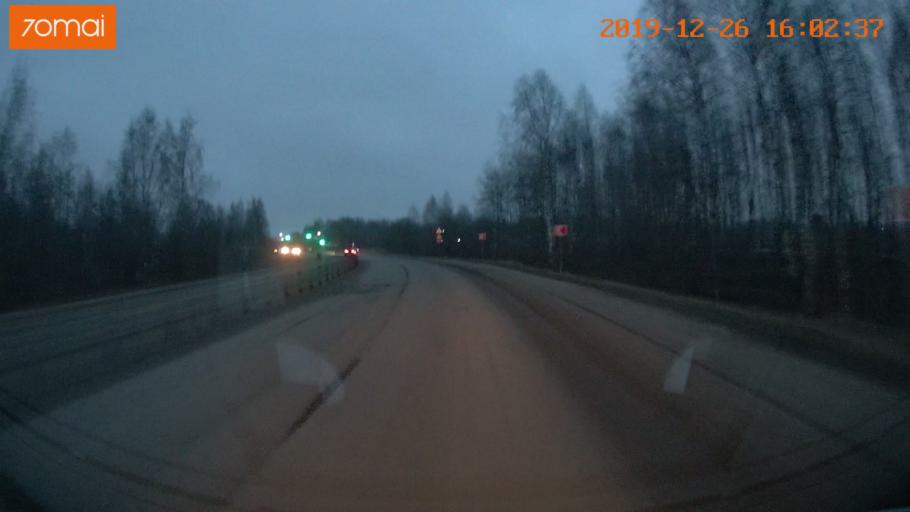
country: RU
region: Jaroslavl
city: Rybinsk
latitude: 58.0106
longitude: 38.8386
